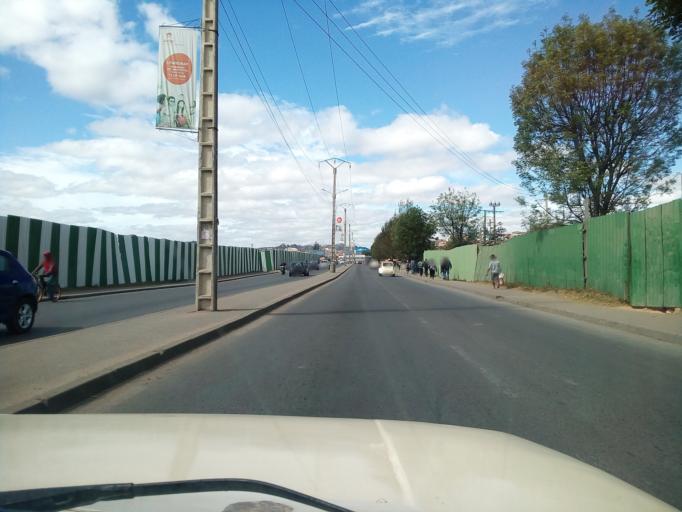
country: MG
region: Analamanga
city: Antananarivo
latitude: -18.8931
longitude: 47.5191
